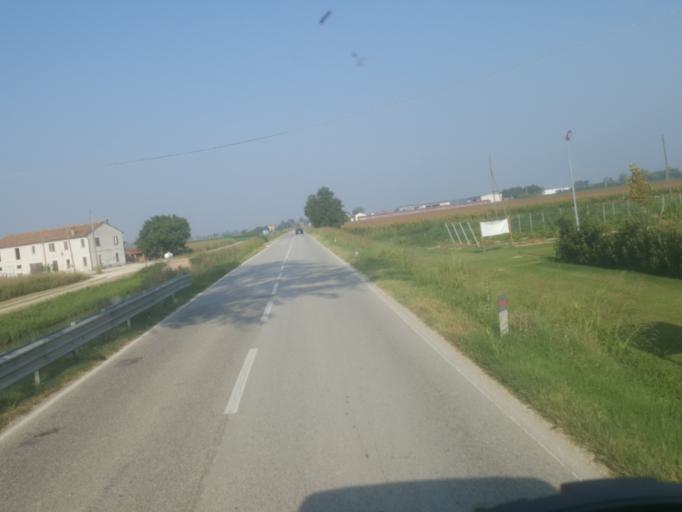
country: IT
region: Emilia-Romagna
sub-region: Provincia di Ravenna
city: Voltana
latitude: 44.5578
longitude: 11.9223
